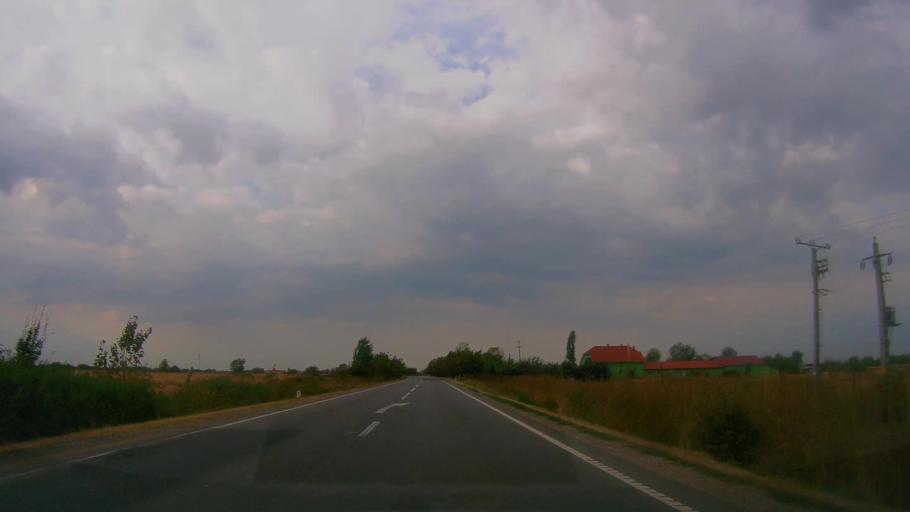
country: RO
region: Satu Mare
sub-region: Comuna Botiz
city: Botiz
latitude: 47.8483
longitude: 22.9694
